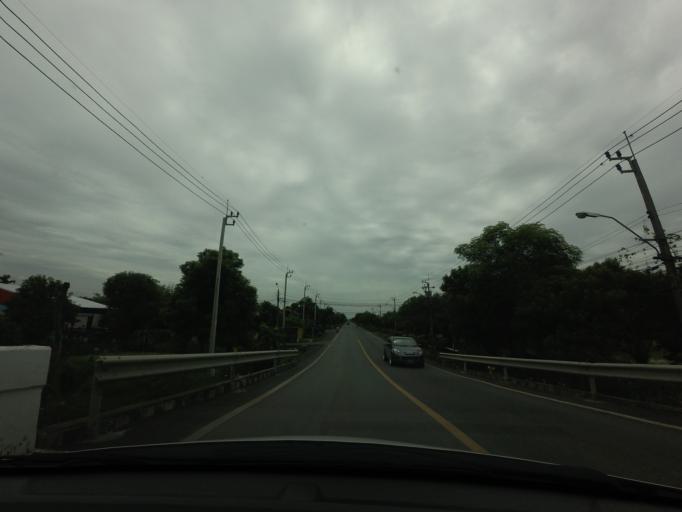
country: TH
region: Bangkok
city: Nong Chok
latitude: 13.8908
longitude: 100.8089
